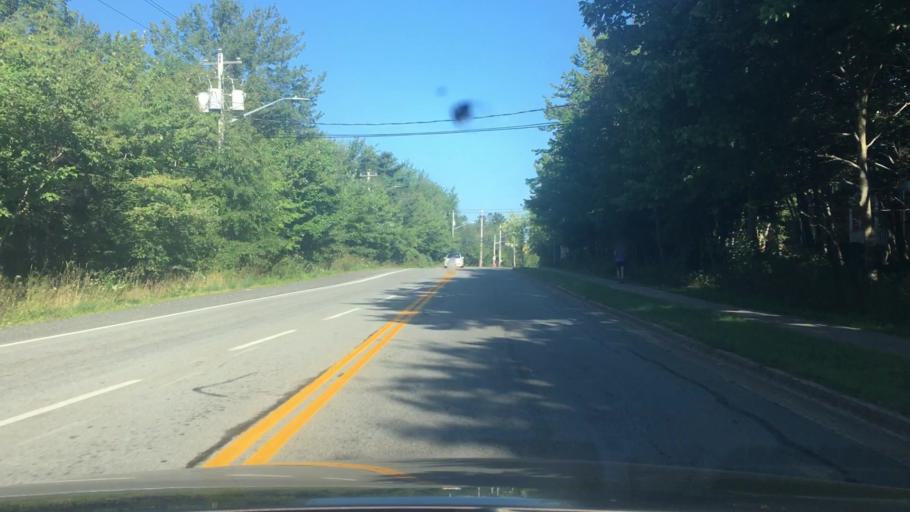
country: CA
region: Nova Scotia
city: Dartmouth
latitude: 44.7174
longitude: -63.6836
